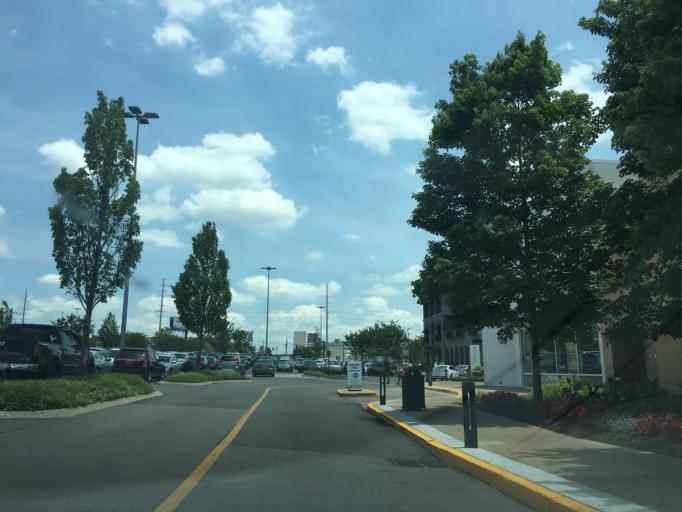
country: US
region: Tennessee
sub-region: Davidson County
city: Oak Hill
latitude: 36.1080
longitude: -86.8149
